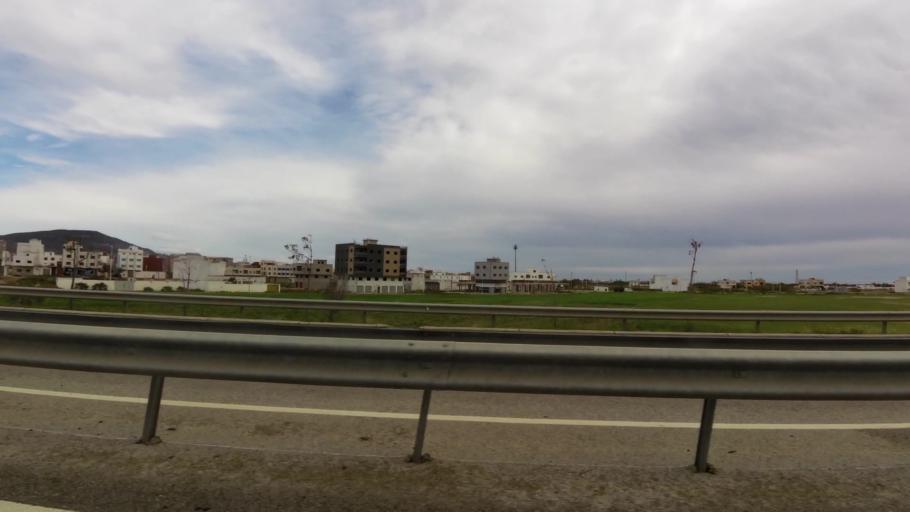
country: MA
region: Tanger-Tetouan
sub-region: Tetouan
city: Martil
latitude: 35.6933
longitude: -5.3461
